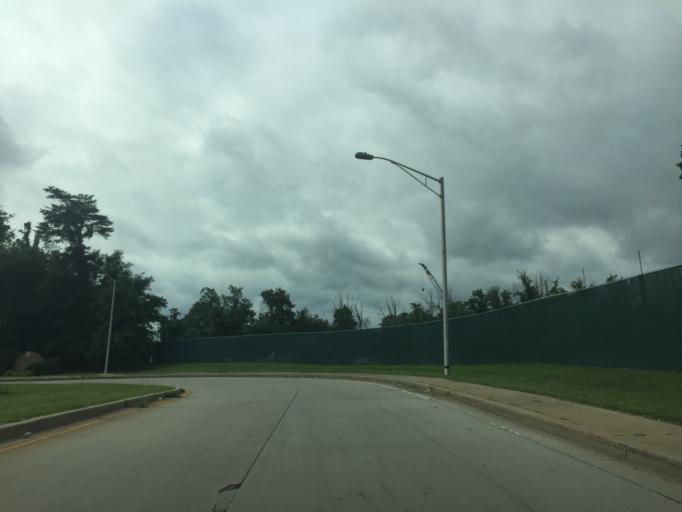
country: US
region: Maryland
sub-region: Anne Arundel County
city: Riviera Beach
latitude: 39.2003
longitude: -76.5566
